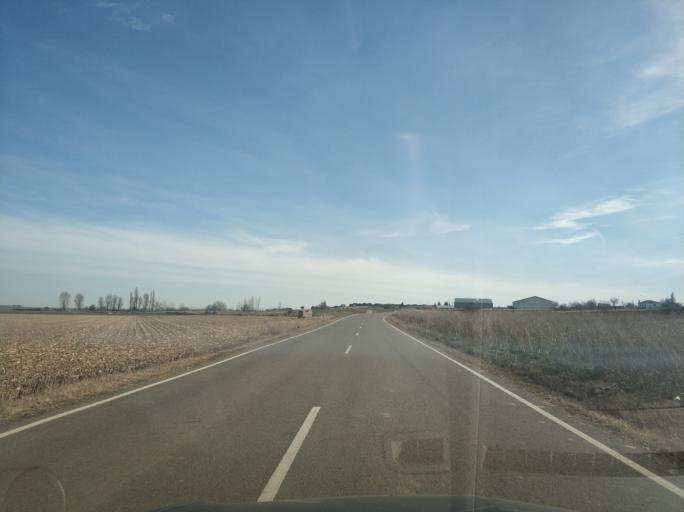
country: ES
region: Castille and Leon
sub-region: Provincia de Salamanca
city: Florida de Liebana
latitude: 41.0318
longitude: -5.7658
